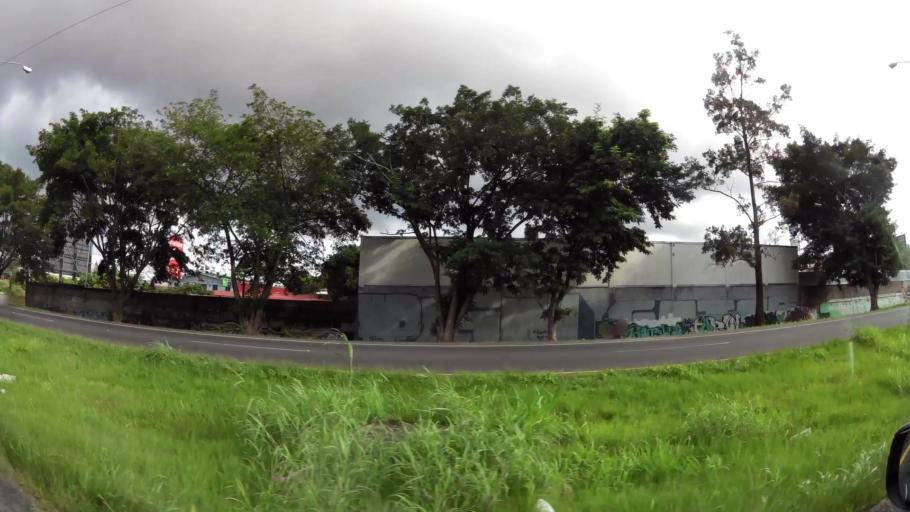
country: CR
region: San Jose
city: Curridabat
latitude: 9.9113
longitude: -84.0214
